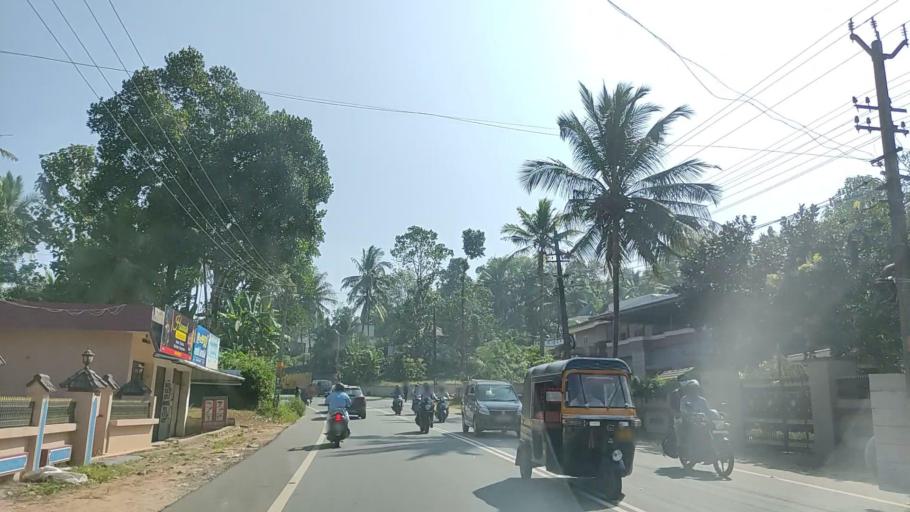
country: IN
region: Kerala
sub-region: Kollam
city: Punalur
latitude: 8.9327
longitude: 76.9389
